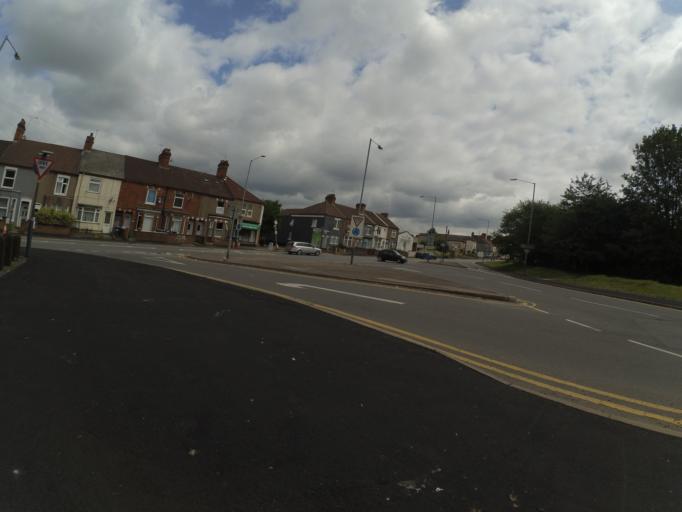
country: GB
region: England
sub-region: Warwickshire
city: Rugby
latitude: 52.3744
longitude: -1.2798
